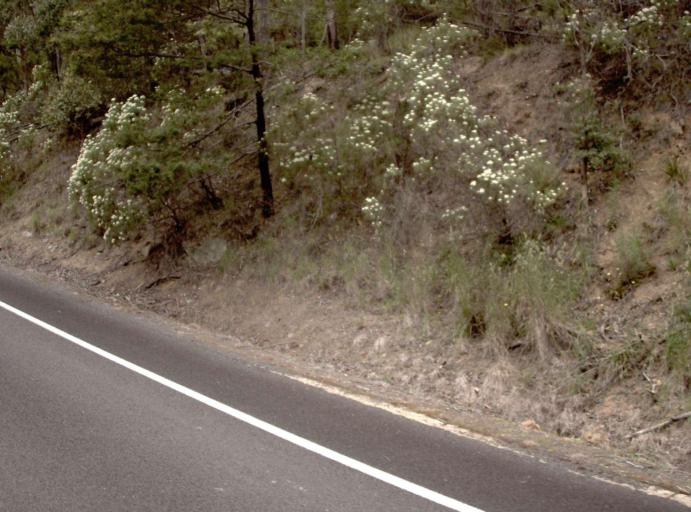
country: AU
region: New South Wales
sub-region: Bombala
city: Bombala
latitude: -37.2528
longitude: 149.2471
